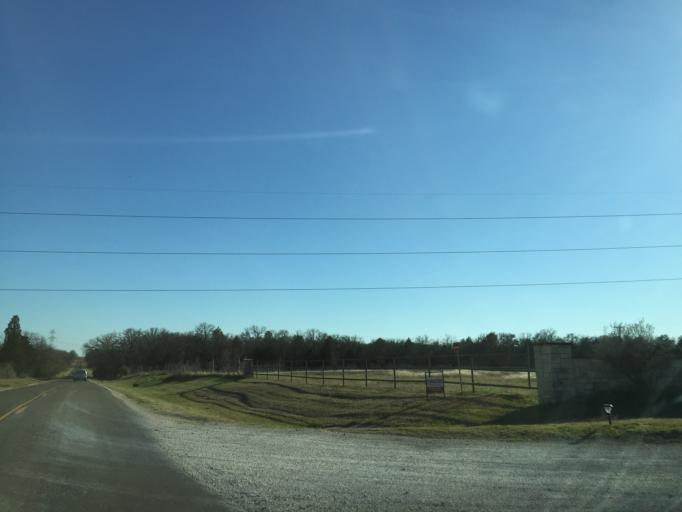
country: US
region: Texas
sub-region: Bastrop County
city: Elgin
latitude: 30.4242
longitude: -97.2594
